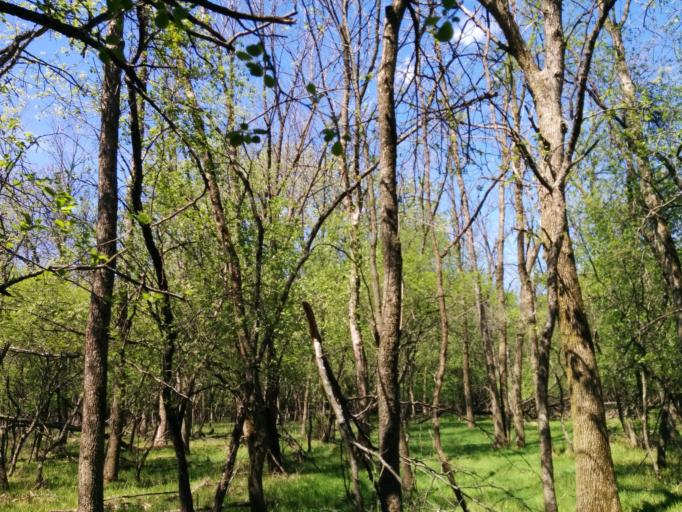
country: US
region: Illinois
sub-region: Cook County
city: Norridge
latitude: 41.9679
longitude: -87.8482
